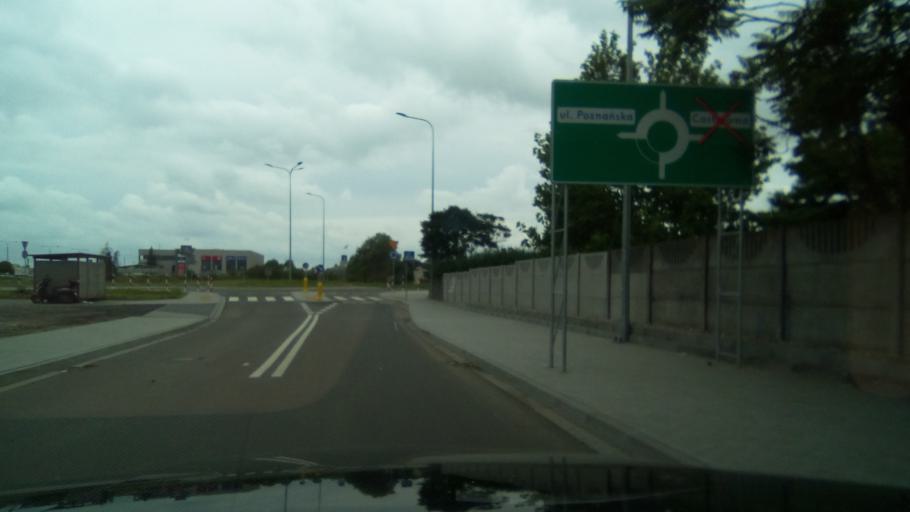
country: PL
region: Greater Poland Voivodeship
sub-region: Powiat gnieznienski
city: Gniezno
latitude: 52.5336
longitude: 17.5581
